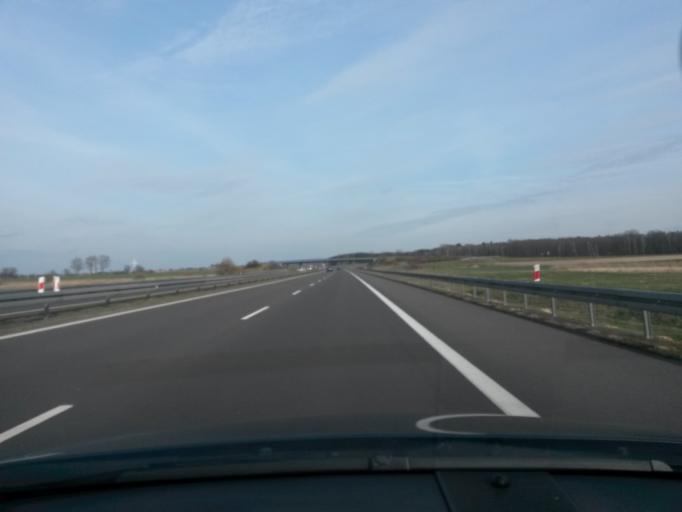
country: PL
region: Greater Poland Voivodeship
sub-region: Powiat sredzki
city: Dominowo
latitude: 52.3098
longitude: 17.3514
